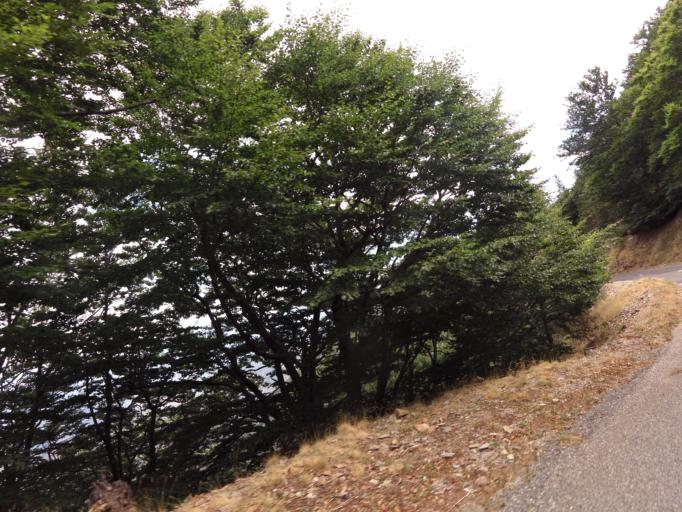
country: FR
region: Languedoc-Roussillon
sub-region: Departement du Gard
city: Valleraugue
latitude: 44.0512
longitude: 3.6067
